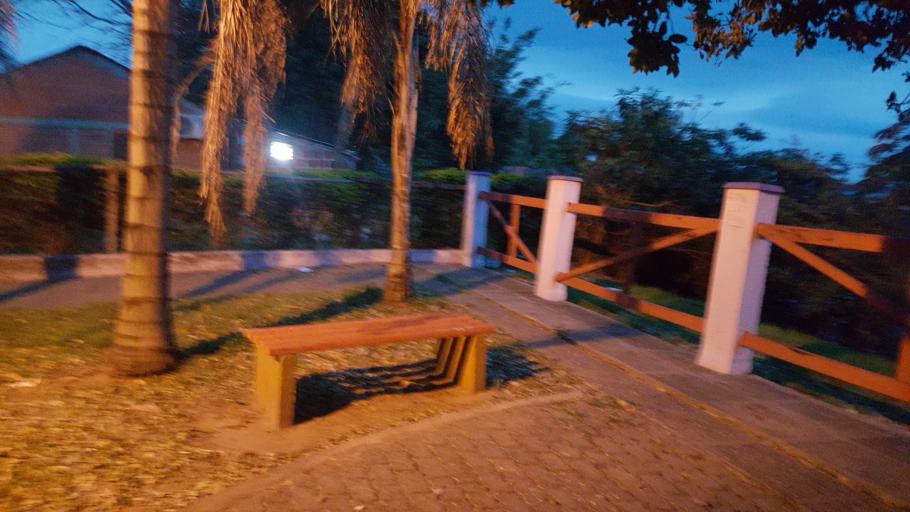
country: AR
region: Corrientes
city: Ituzaingo
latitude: -27.5843
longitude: -56.6901
